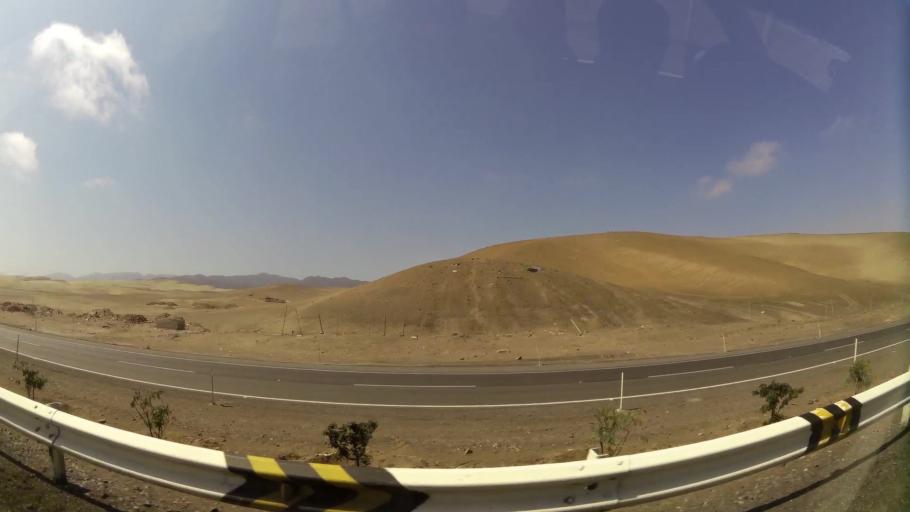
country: PE
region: Lima
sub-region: Provincia de Canete
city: Quilmana
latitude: -12.9094
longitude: -76.5013
